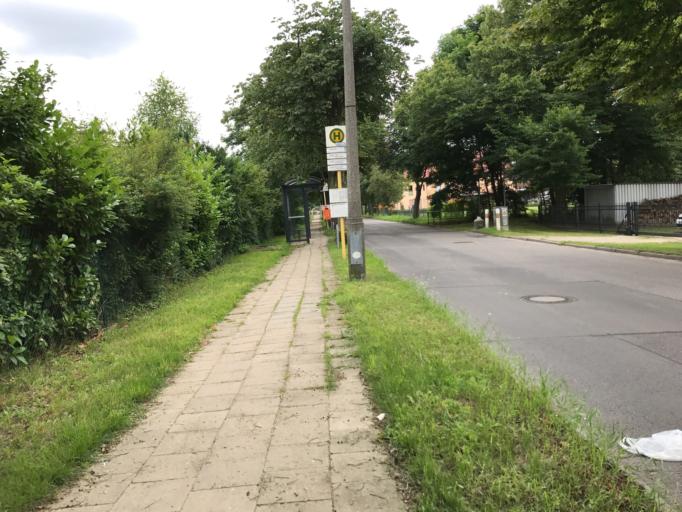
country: DE
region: Berlin
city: Karow
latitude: 52.6124
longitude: 13.4803
